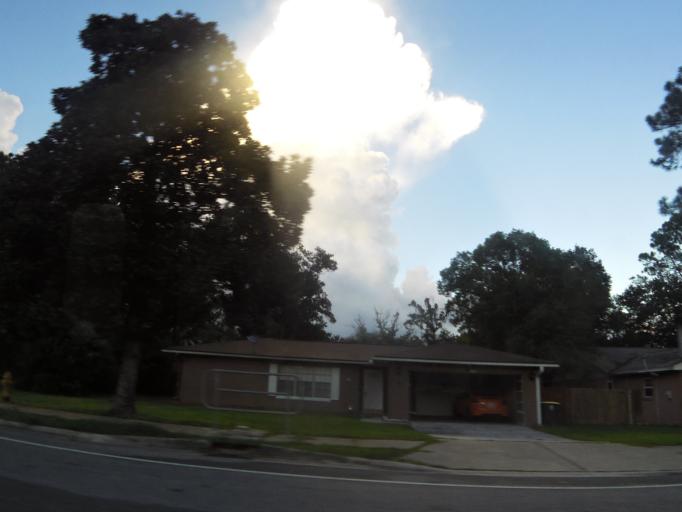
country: US
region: Florida
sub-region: Duval County
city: Jacksonville
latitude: 30.2380
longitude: -81.6071
